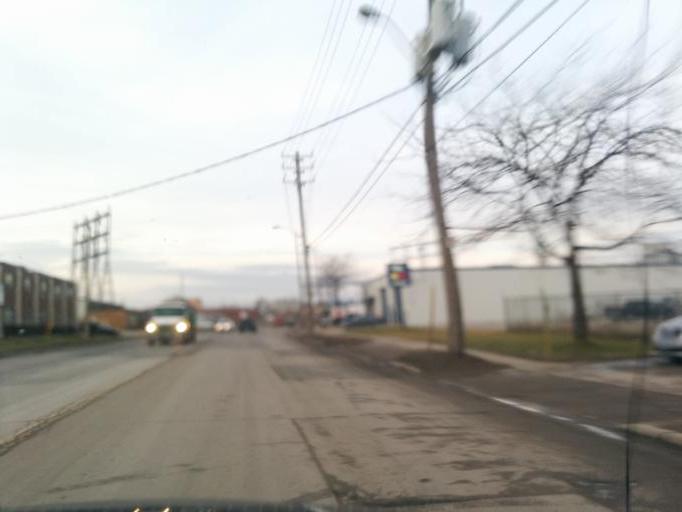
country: CA
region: Ontario
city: Etobicoke
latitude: 43.6279
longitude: -79.5429
